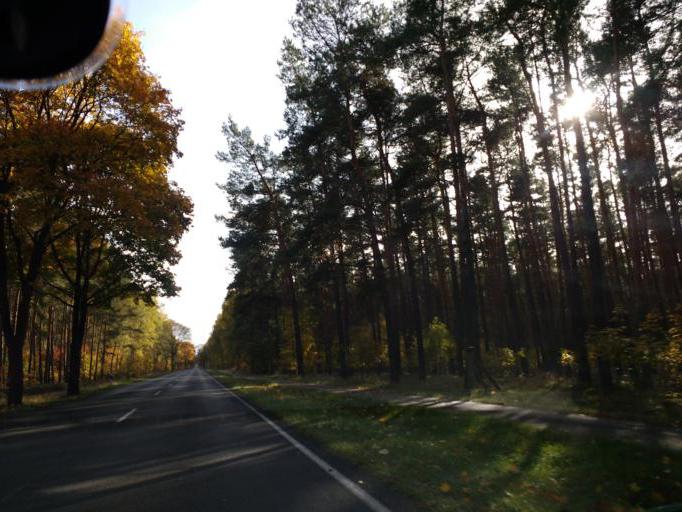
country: DE
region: Brandenburg
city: Grunheide
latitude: 52.3838
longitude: 13.8299
